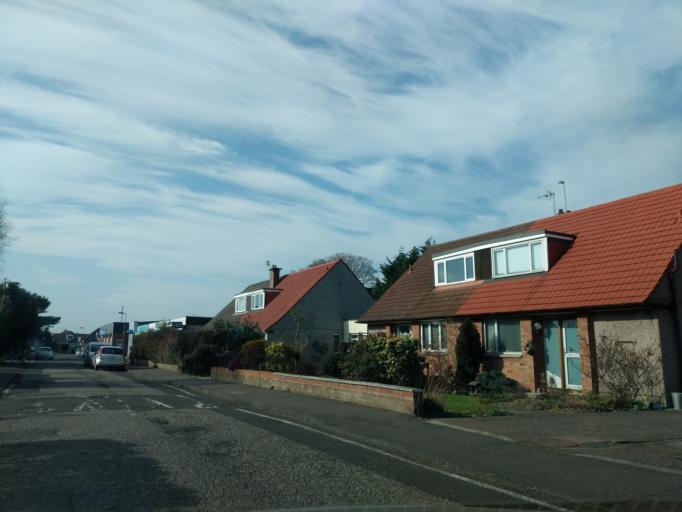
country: GB
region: Scotland
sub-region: Edinburgh
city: Currie
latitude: 55.9513
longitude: -3.2941
